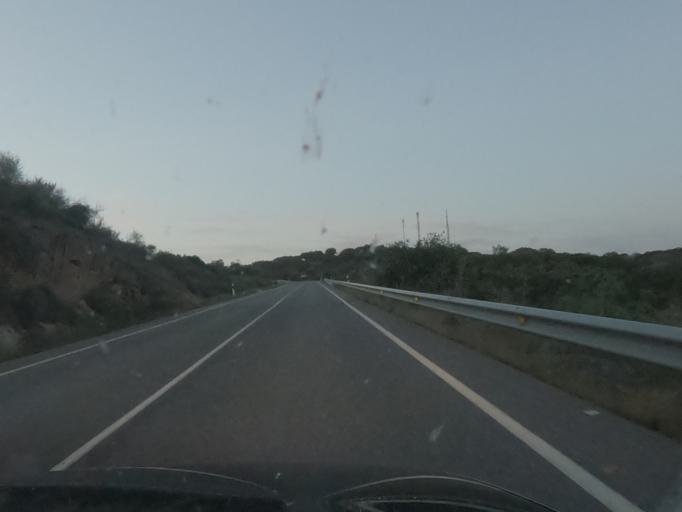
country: ES
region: Extremadura
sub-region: Provincia de Caceres
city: Alcantara
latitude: 39.7435
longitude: -6.9016
